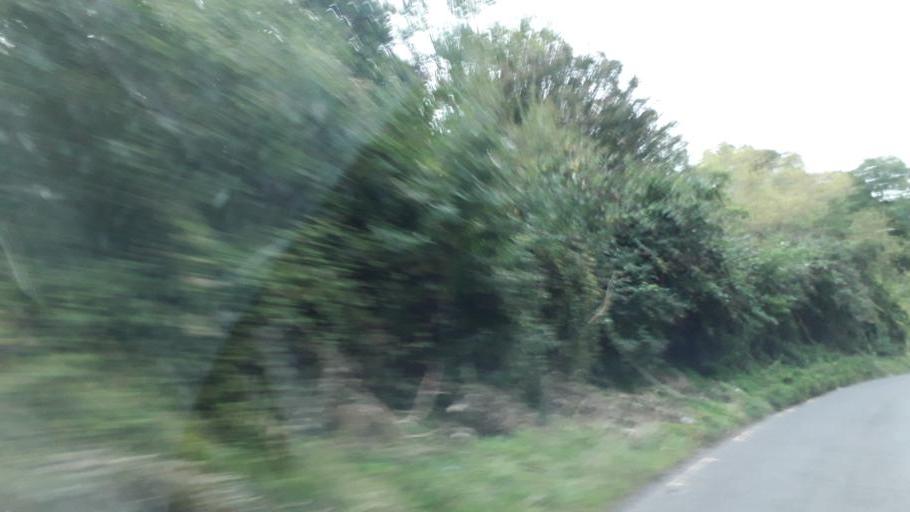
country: IE
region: Leinster
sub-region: Wicklow
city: Enniskerry
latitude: 53.1925
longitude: -6.1607
